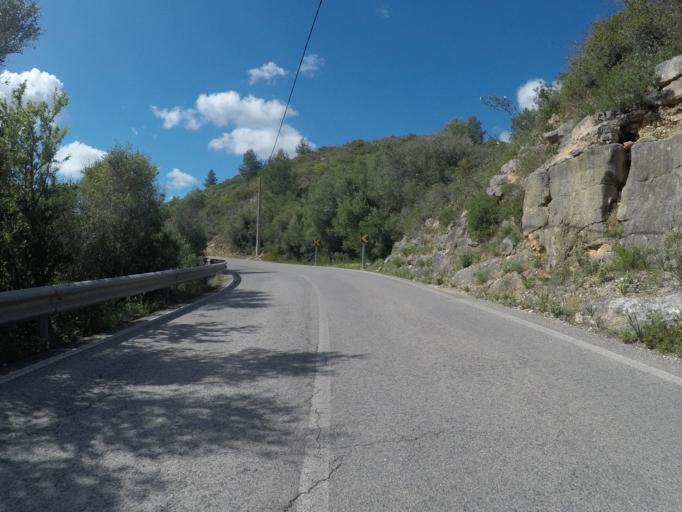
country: PT
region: Faro
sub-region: Vila do Bispo
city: Vila do Bispo
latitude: 37.0693
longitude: -8.8251
